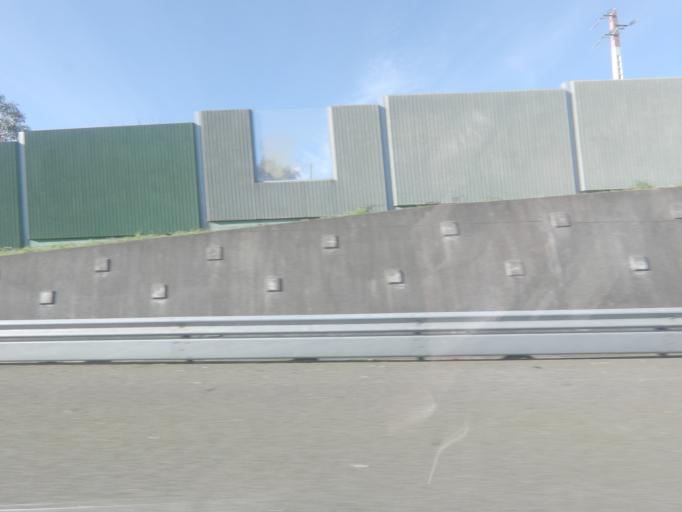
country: PT
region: Aveiro
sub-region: Ovar
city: Sao Joao
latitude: 40.8842
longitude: -8.5638
